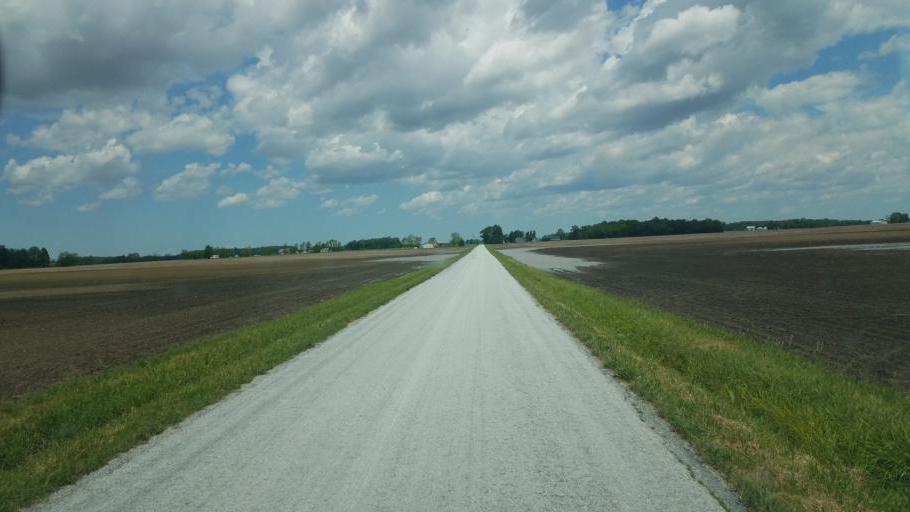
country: US
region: Ohio
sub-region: Hardin County
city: Forest
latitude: 40.6736
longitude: -83.4776
